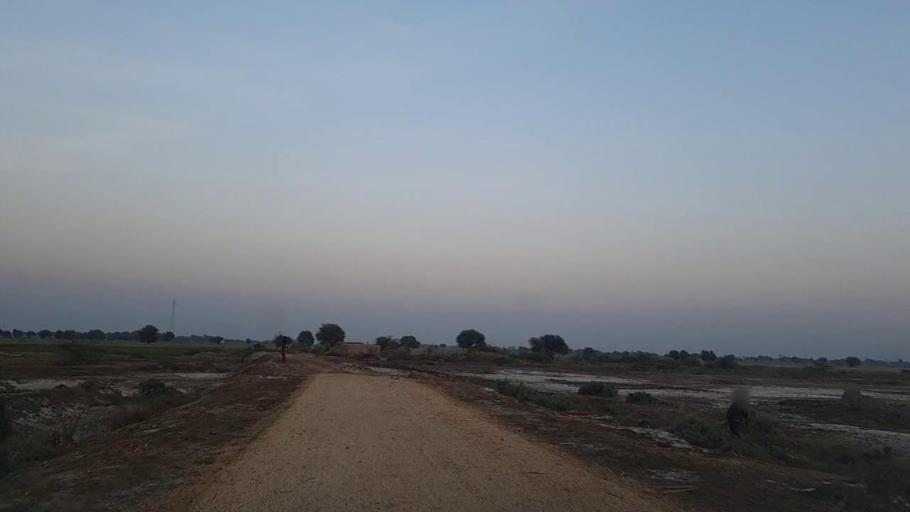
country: PK
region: Sindh
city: Naukot
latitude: 24.9792
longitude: 69.4334
